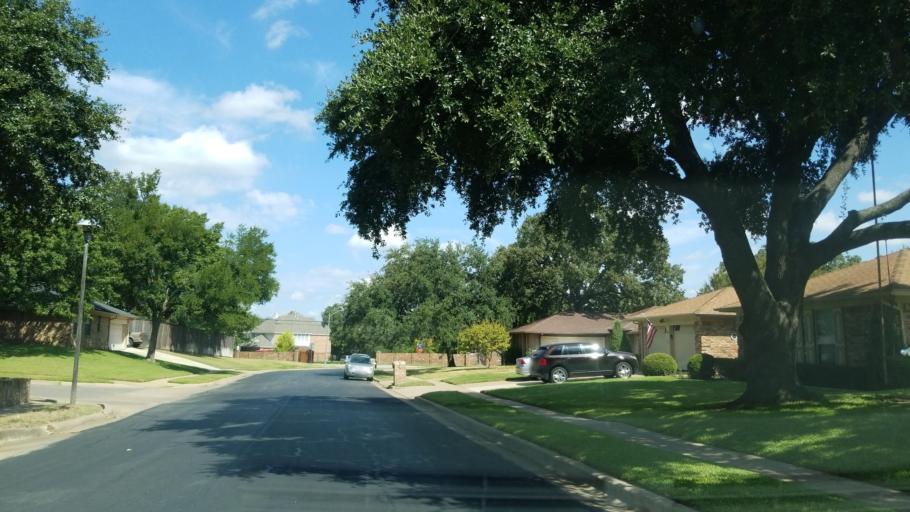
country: US
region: Texas
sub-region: Tarrant County
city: Euless
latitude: 32.8583
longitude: -97.0968
